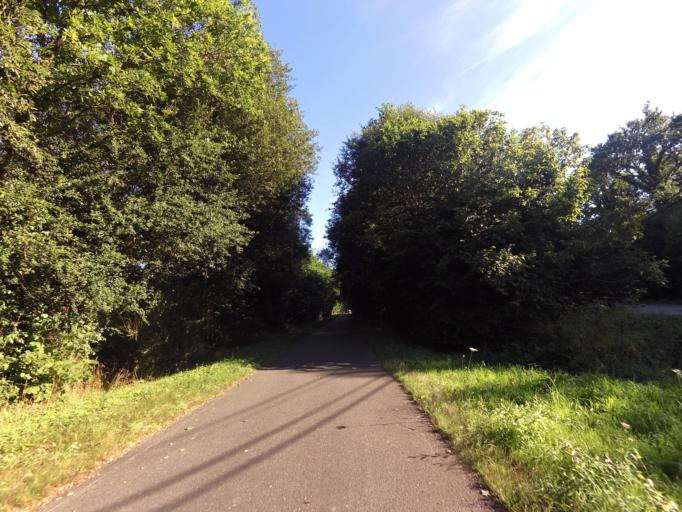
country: FR
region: Brittany
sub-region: Departement du Morbihan
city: Guillac
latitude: 47.8769
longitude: -2.4373
